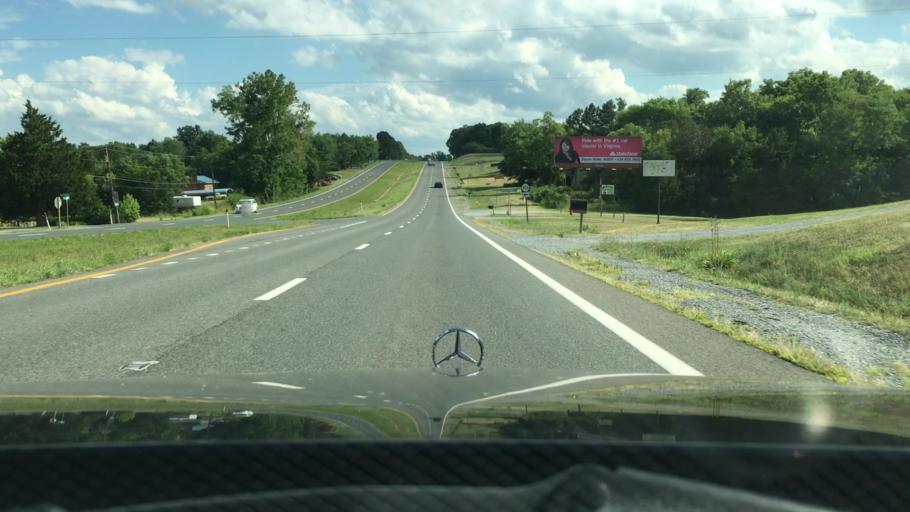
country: US
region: Virginia
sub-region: Campbell County
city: Altavista
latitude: 37.1825
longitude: -79.2047
